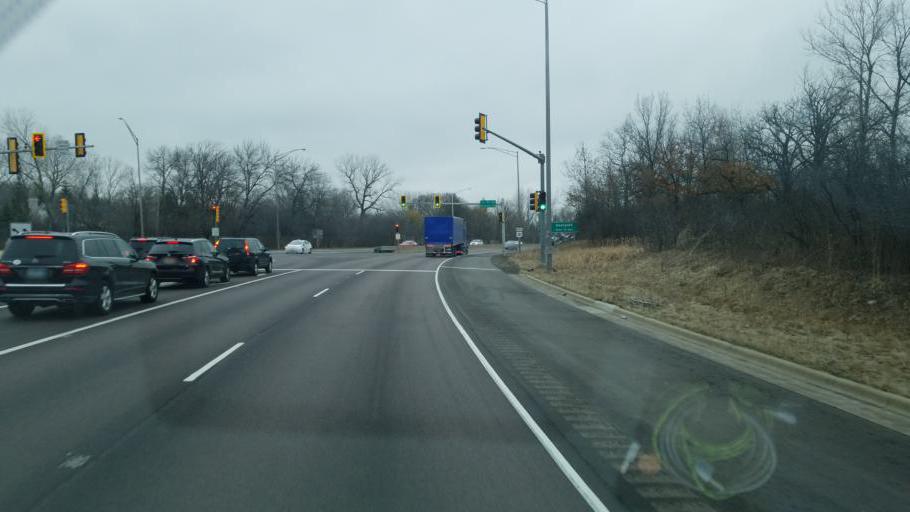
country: US
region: Illinois
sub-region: Lake County
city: Lake Forest
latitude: 42.2394
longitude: -87.8619
